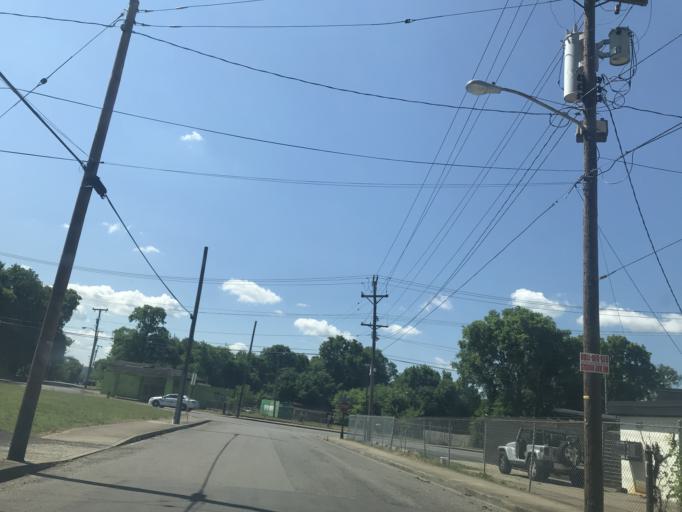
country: US
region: Tennessee
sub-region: Davidson County
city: Nashville
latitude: 36.1808
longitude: -86.8068
